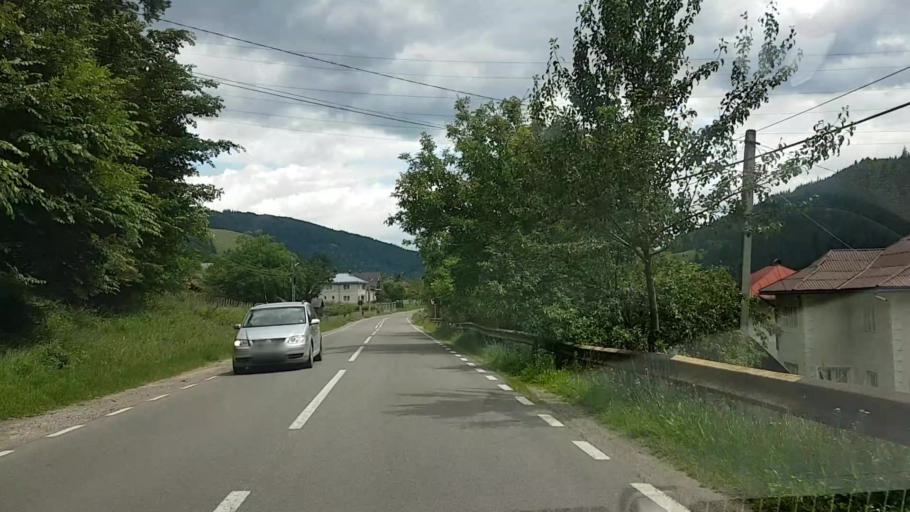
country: RO
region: Neamt
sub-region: Comuna Poiana Teiului
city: Poiana Teiului
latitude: 47.1191
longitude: 25.9155
